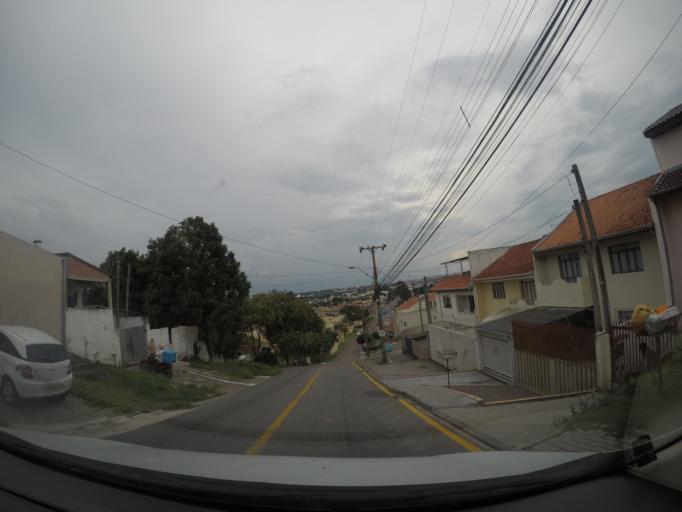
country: BR
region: Parana
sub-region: Curitiba
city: Curitiba
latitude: -25.4690
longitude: -49.2426
